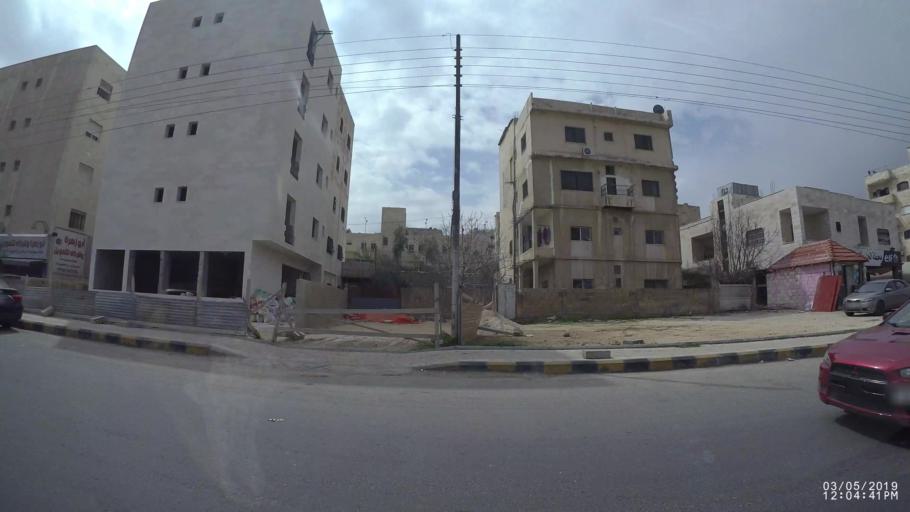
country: JO
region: Amman
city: Amman
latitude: 31.9757
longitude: 35.9199
